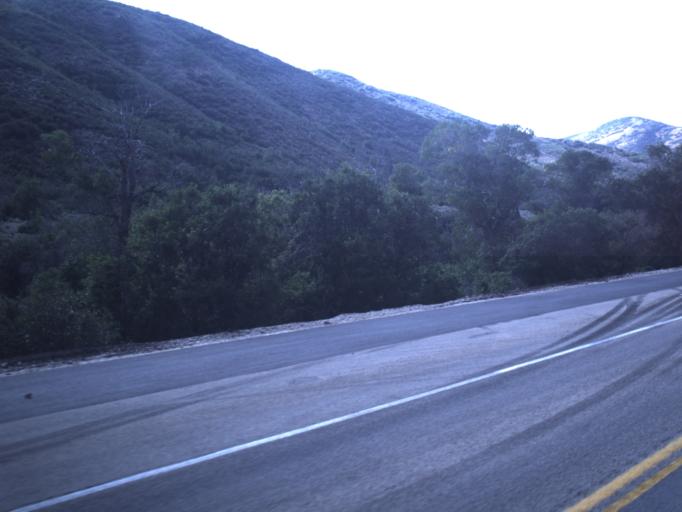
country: US
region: Utah
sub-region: Wasatch County
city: Heber
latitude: 40.4250
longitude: -111.3460
